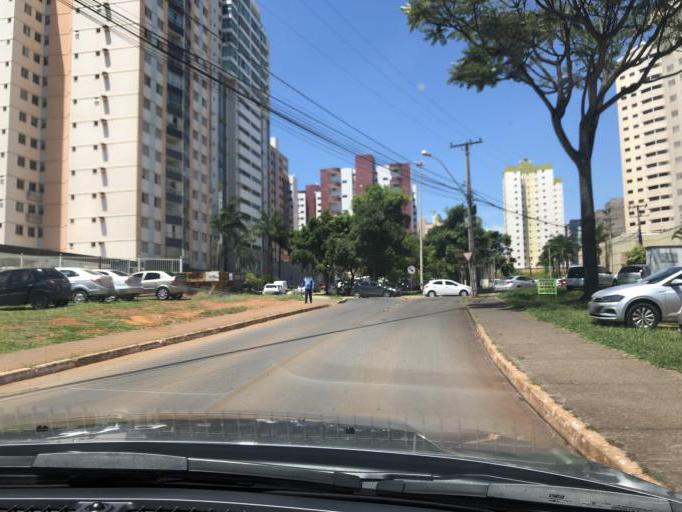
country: BR
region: Federal District
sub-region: Brasilia
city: Brasilia
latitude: -15.8320
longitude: -48.0126
